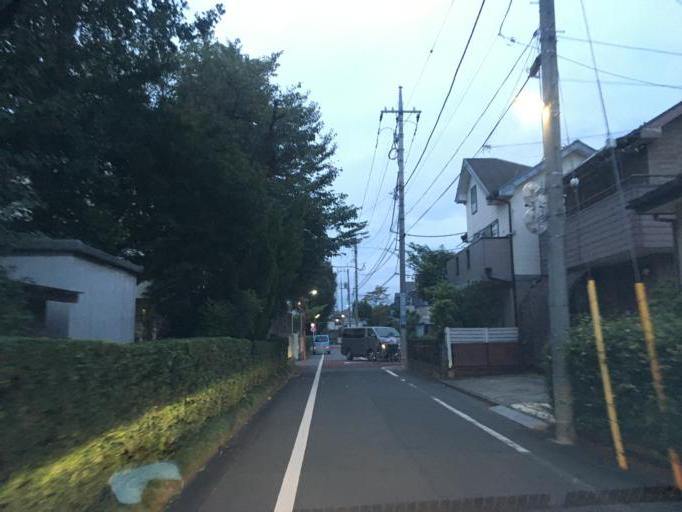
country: JP
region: Tokyo
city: Kokubunji
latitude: 35.7149
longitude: 139.4555
